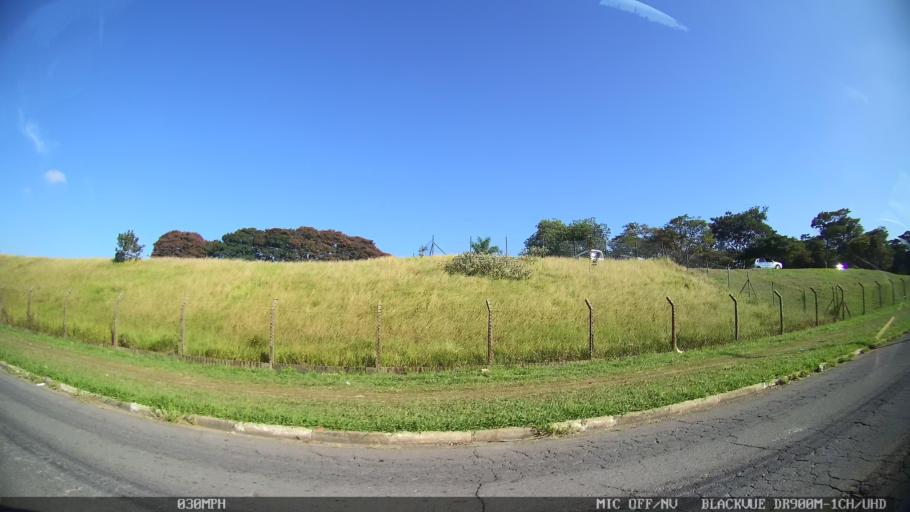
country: BR
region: Sao Paulo
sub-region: Campinas
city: Campinas
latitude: -22.9939
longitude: -47.1120
